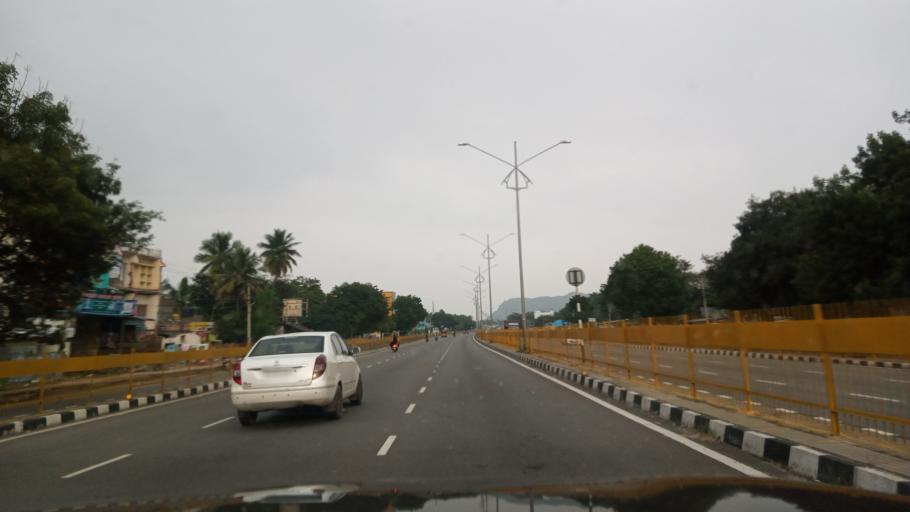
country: IN
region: Tamil Nadu
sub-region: Vellore
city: Katpadi
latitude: 12.9411
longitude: 79.1778
